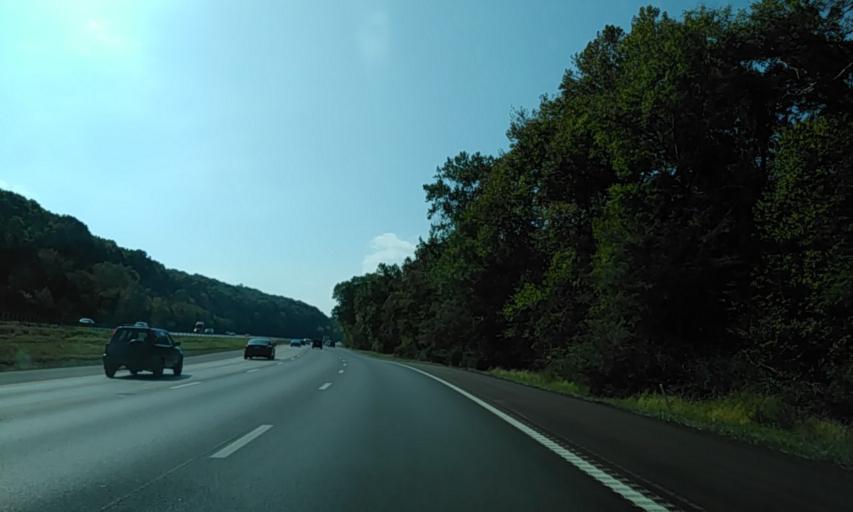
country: US
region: Missouri
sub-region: Saint Louis County
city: Valley Park
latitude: 38.5242
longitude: -90.5449
